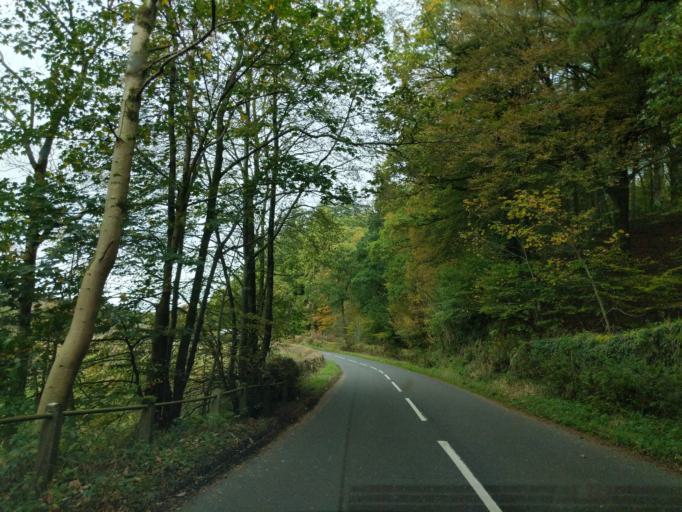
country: GB
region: Scotland
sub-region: Dumfries and Galloway
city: Thornhill
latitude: 55.2652
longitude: -3.7791
